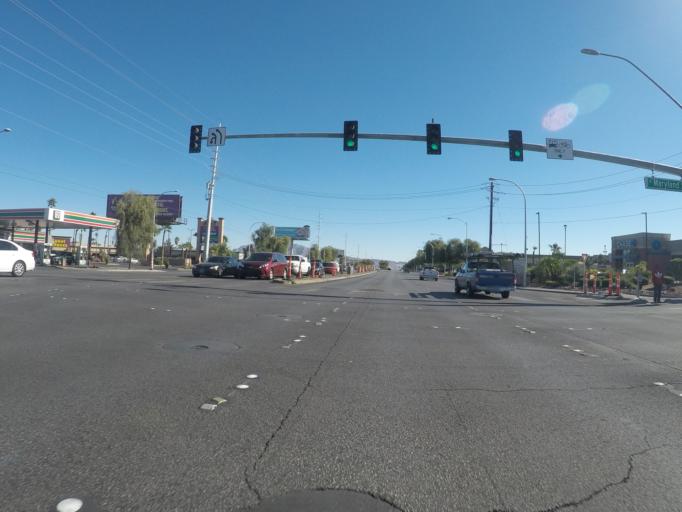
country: US
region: Nevada
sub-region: Clark County
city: Winchester
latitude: 36.1442
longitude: -115.1370
